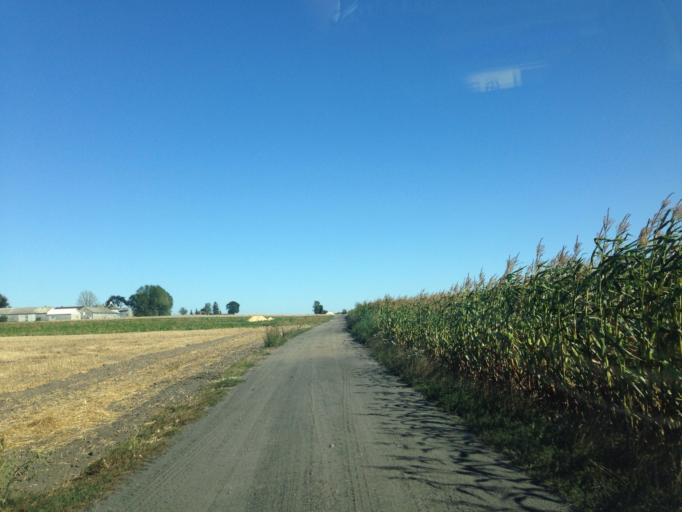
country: PL
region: Kujawsko-Pomorskie
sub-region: Powiat brodnicki
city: Brodnica
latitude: 53.2103
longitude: 19.4189
